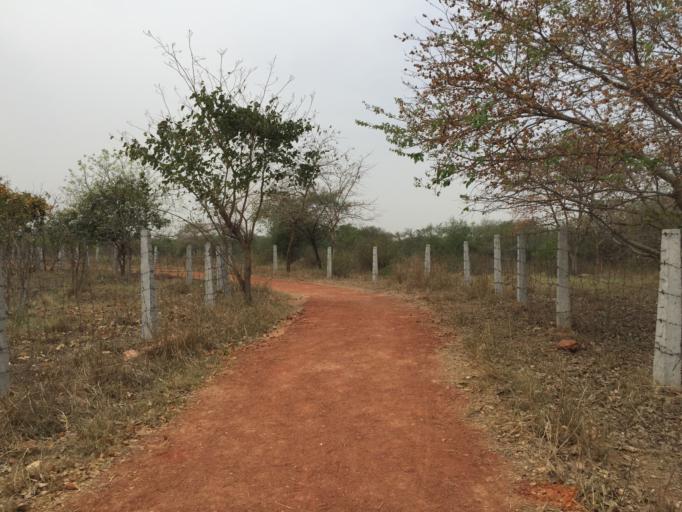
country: IN
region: NCT
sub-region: Central Delhi
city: Karol Bagh
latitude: 28.5481
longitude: 77.1491
